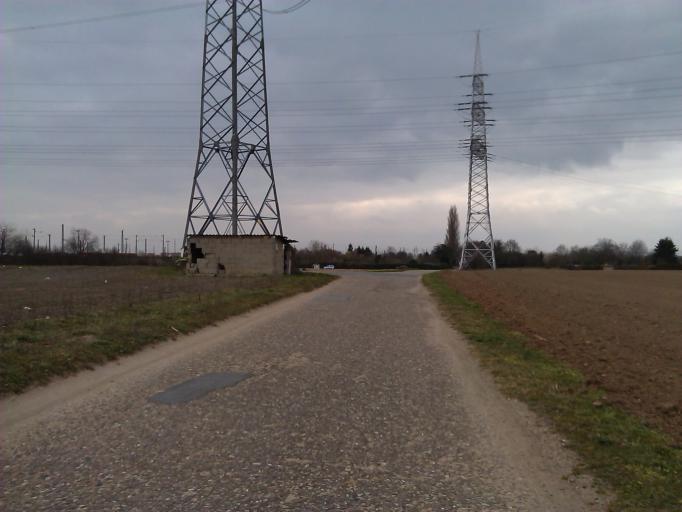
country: DE
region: Hesse
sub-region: Regierungsbezirk Darmstadt
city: Bischofsheim
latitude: 49.9821
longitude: 8.3814
